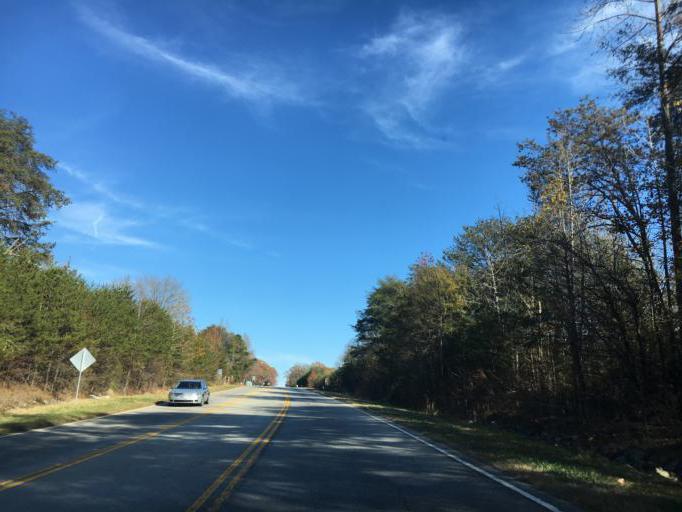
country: US
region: South Carolina
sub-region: Spartanburg County
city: Wellford
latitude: 34.9599
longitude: -82.0744
